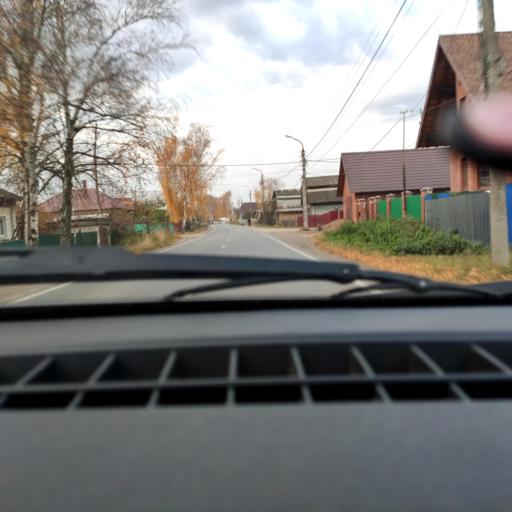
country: RU
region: Bashkortostan
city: Iglino
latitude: 54.8316
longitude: 56.1909
